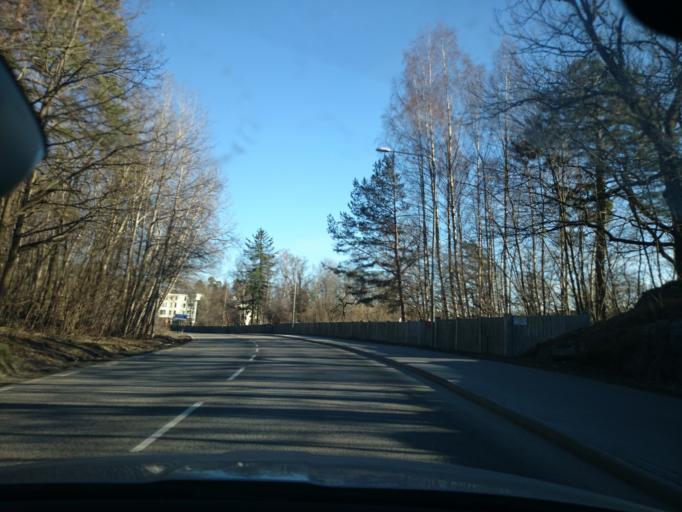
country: SE
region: Stockholm
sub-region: Stockholms Kommun
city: Arsta
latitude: 59.2522
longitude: 18.0496
